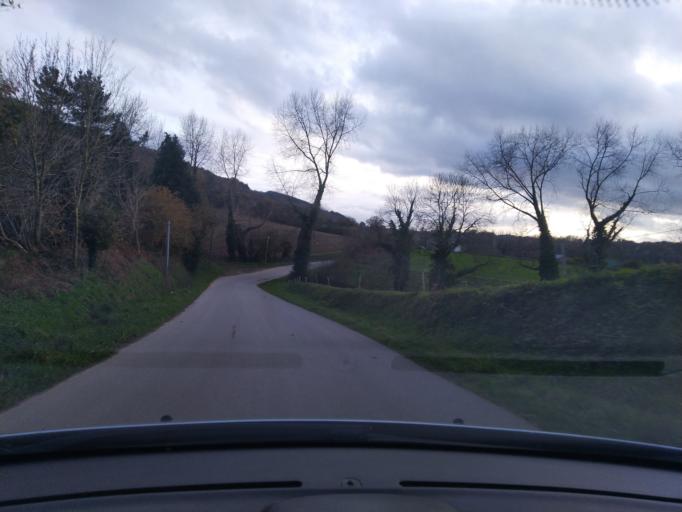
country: FR
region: Brittany
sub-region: Departement du Finistere
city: Guerlesquin
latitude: 48.5606
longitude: -3.6175
